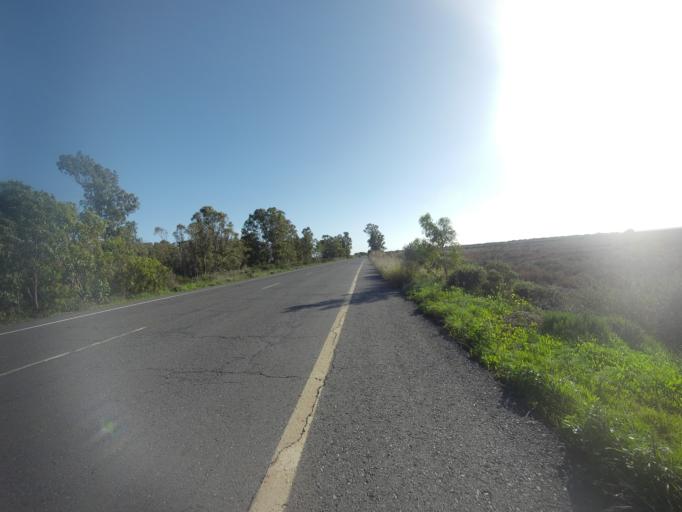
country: ES
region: Andalusia
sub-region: Provincia de Huelva
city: Huelva
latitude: 37.2394
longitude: -6.9649
